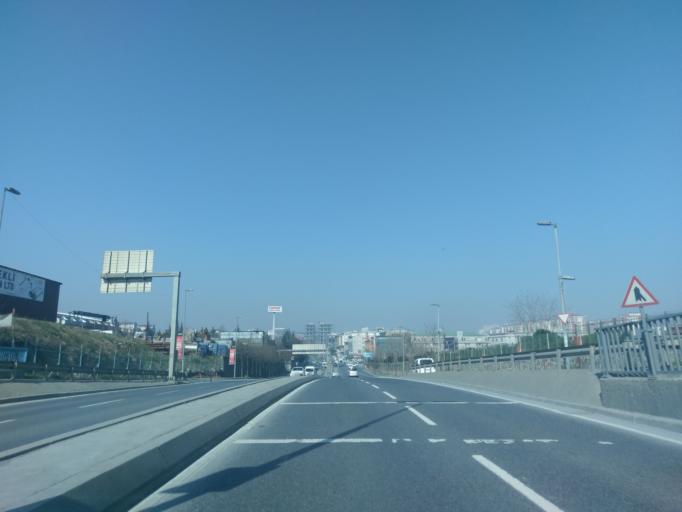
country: TR
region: Istanbul
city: Basaksehir
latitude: 41.0823
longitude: 28.8060
